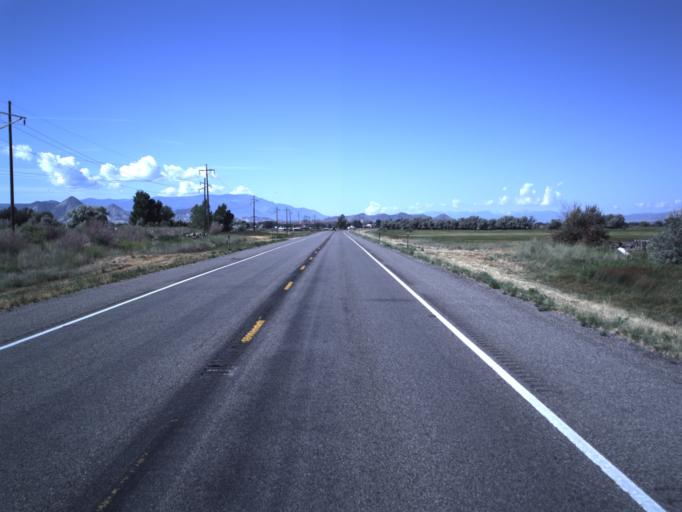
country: US
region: Utah
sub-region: Sevier County
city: Salina
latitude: 38.9855
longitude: -111.8507
